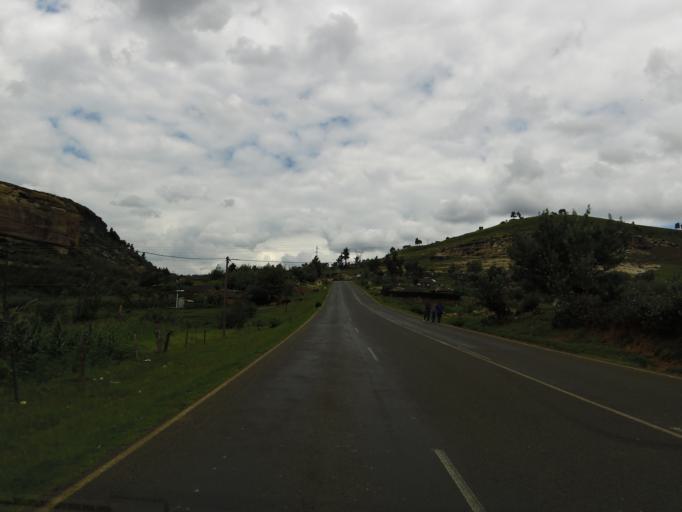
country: LS
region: Leribe
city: Leribe
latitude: -28.9880
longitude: 28.1843
